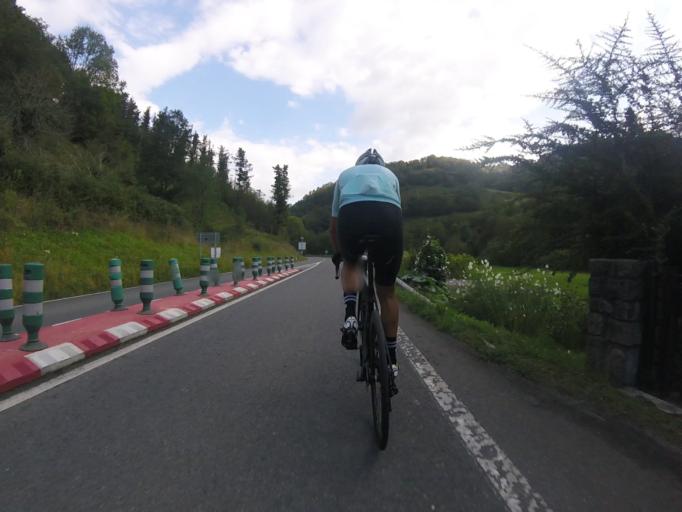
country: ES
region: Basque Country
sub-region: Provincia de Guipuzcoa
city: Amezqueta
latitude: 43.0687
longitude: -2.0844
